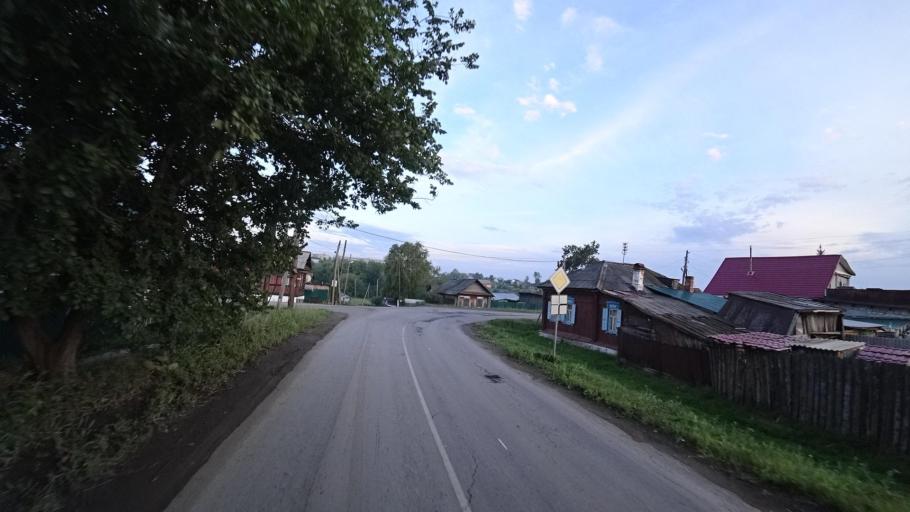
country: RU
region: Sverdlovsk
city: Kamyshlov
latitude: 56.8574
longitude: 62.7080
